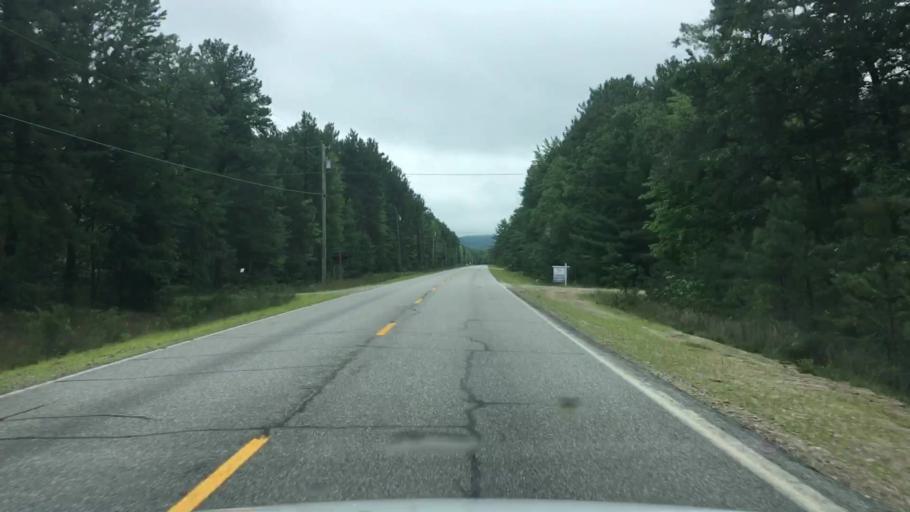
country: US
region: Maine
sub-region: Oxford County
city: Brownfield
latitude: 43.9423
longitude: -70.8874
